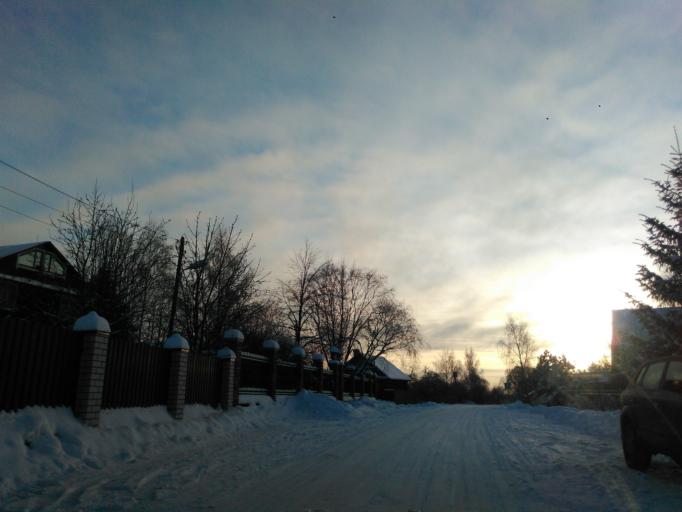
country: RU
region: Tverskaya
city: Zavidovo
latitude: 56.6333
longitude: 36.6145
